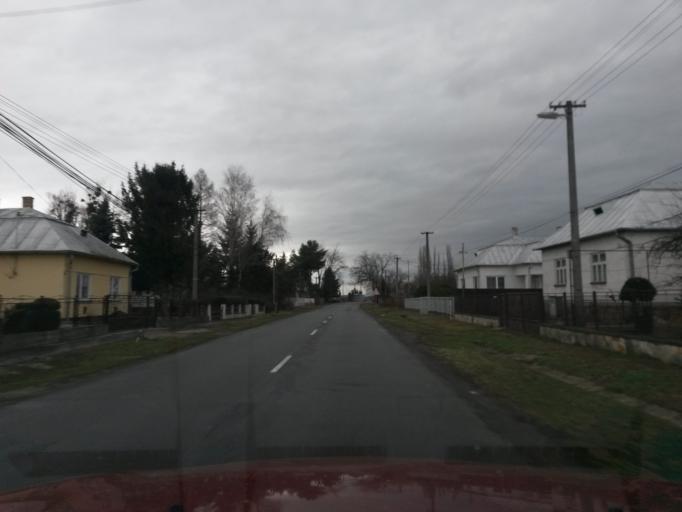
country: SK
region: Kosicky
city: Michalovce
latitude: 48.7099
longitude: 21.9256
